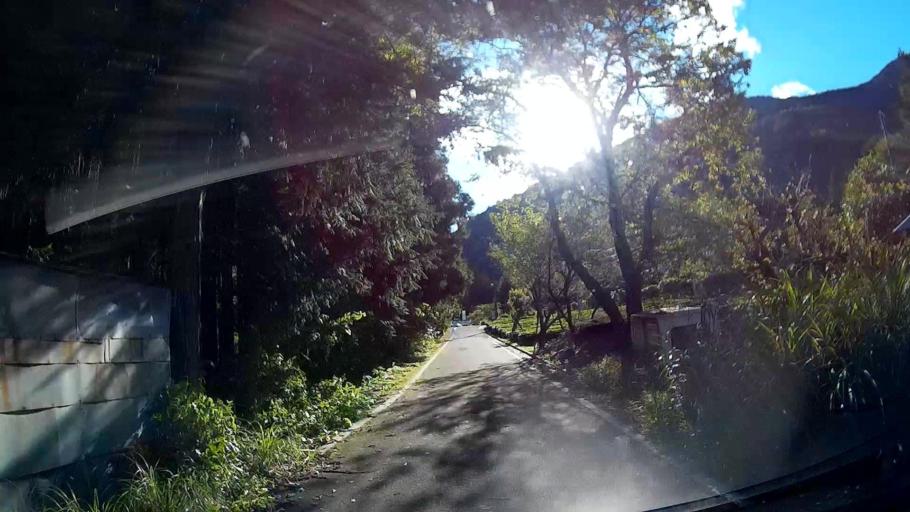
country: JP
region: Shizuoka
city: Shizuoka-shi
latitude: 35.2169
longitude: 138.2235
